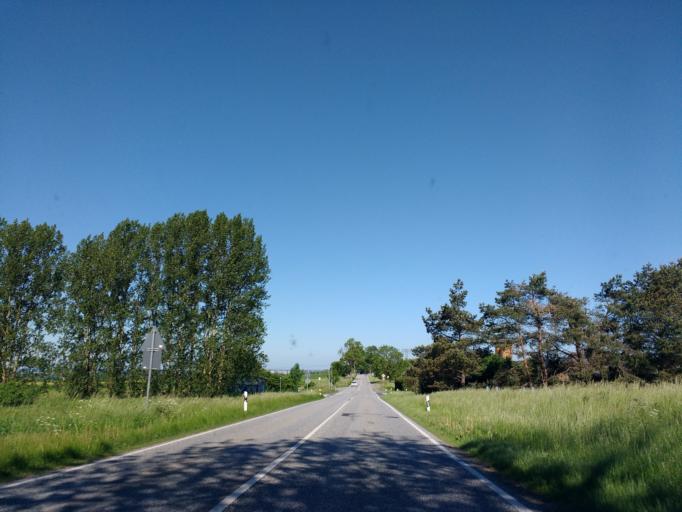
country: DE
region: Mecklenburg-Vorpommern
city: Hornstorf
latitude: 53.8866
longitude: 11.5410
